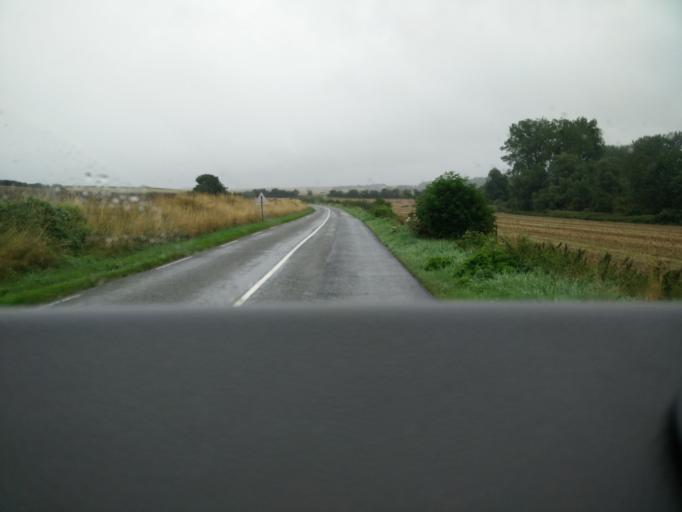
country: FR
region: Picardie
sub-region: Departement de la Somme
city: Nouvion
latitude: 50.2736
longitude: 1.8055
